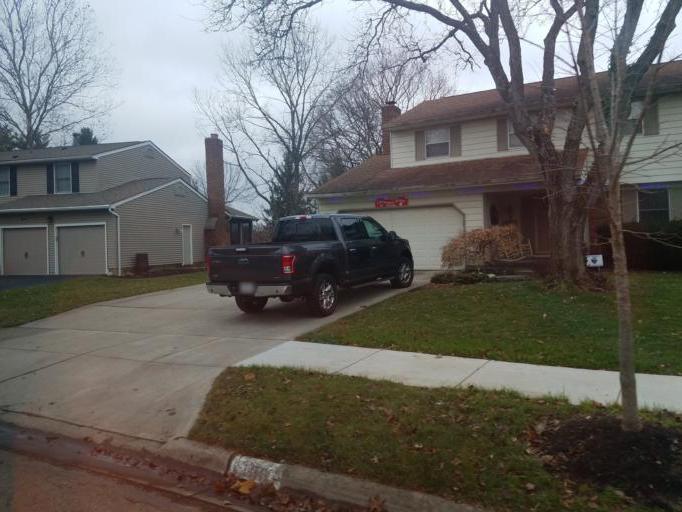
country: US
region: Ohio
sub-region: Franklin County
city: Westerville
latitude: 40.1275
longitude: -82.9610
